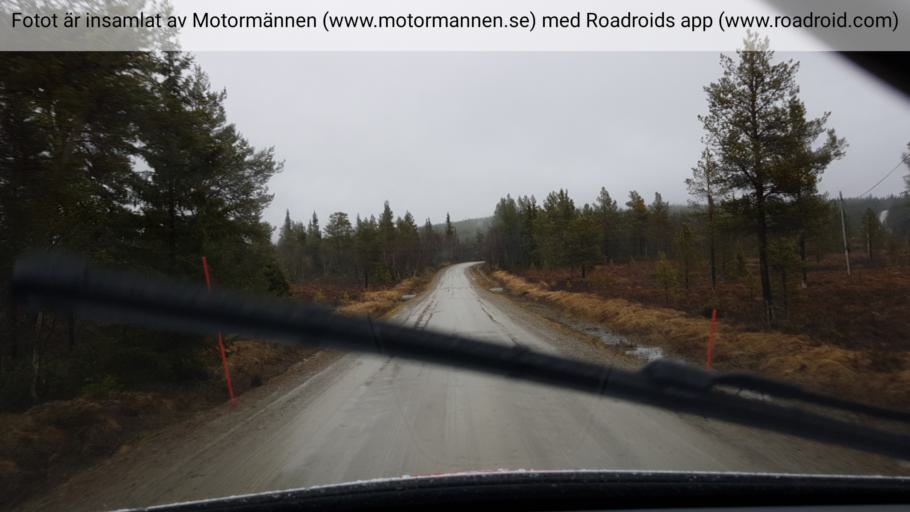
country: SE
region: Jaemtland
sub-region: Are Kommun
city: Jarpen
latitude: 62.5994
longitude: 13.2569
